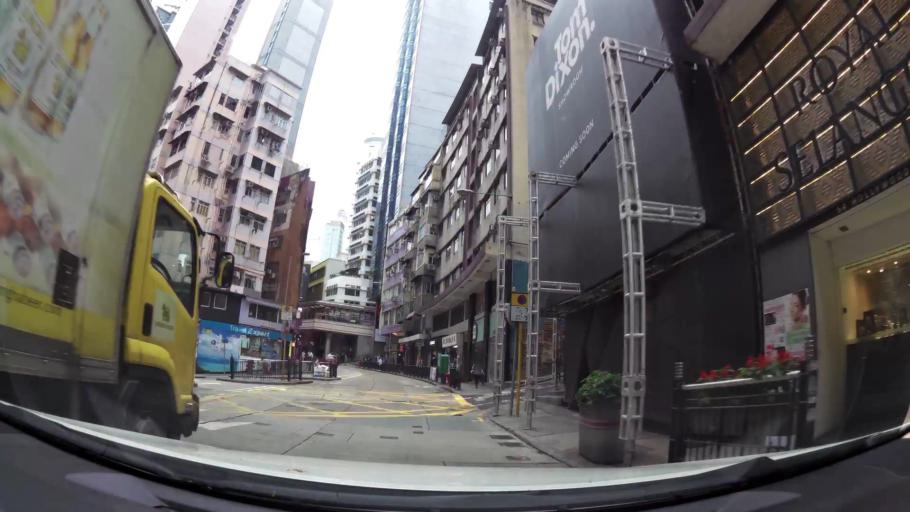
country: HK
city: Hong Kong
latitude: 22.2830
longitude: 114.1526
